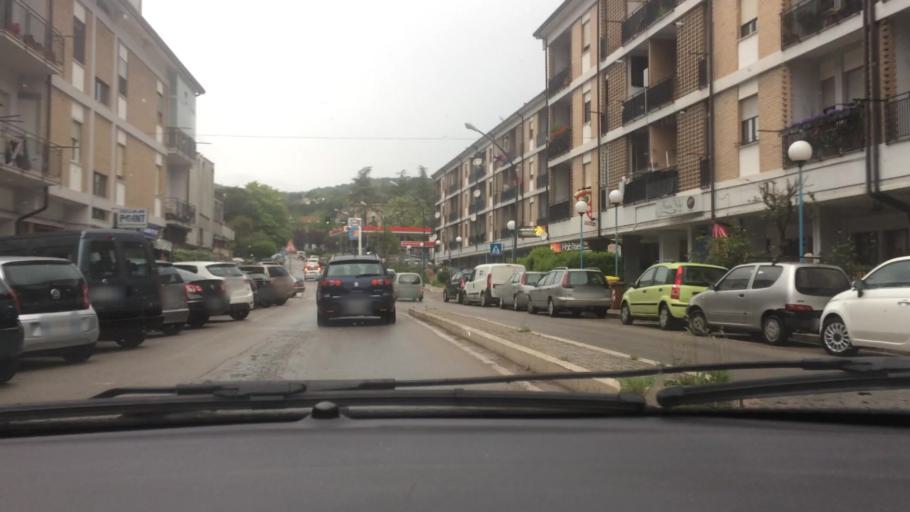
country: IT
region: Basilicate
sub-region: Provincia di Potenza
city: Potenza
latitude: 40.6474
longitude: 15.7973
